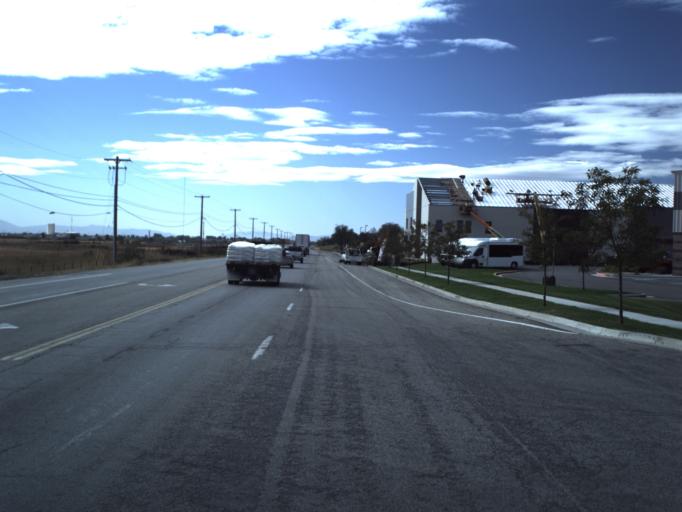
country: US
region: Utah
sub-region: Davis County
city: North Salt Lake
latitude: 40.8302
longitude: -111.9371
